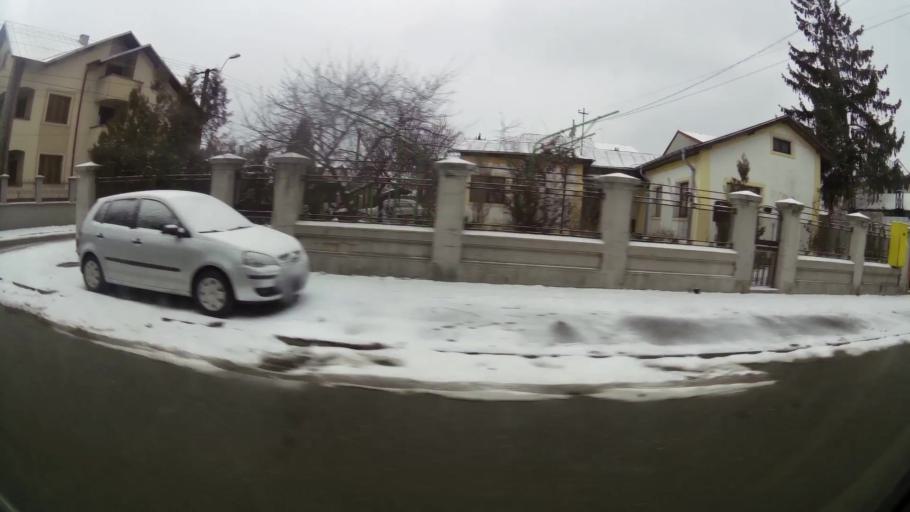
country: RO
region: Prahova
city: Ploiesti
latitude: 44.9327
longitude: 26.0368
